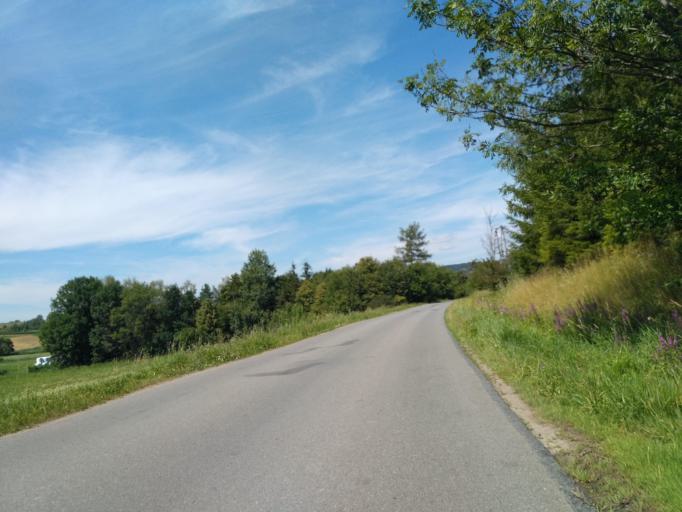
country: PL
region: Subcarpathian Voivodeship
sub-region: Powiat sanocki
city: Nowosielce-Gniewosz
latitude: 49.5461
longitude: 22.1083
